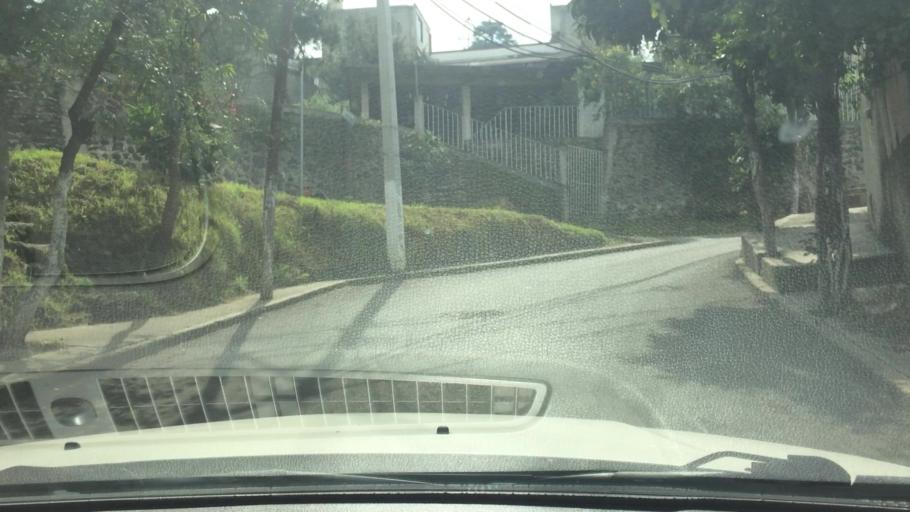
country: MX
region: Mexico City
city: Xochimilco
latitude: 19.2375
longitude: -99.1507
